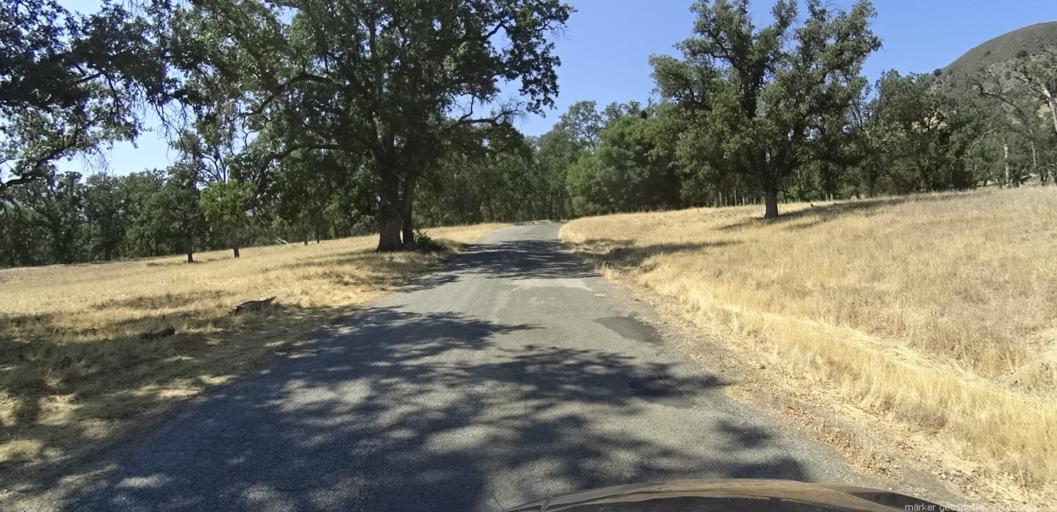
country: US
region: California
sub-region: Monterey County
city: Greenfield
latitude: 36.0886
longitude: -121.4120
